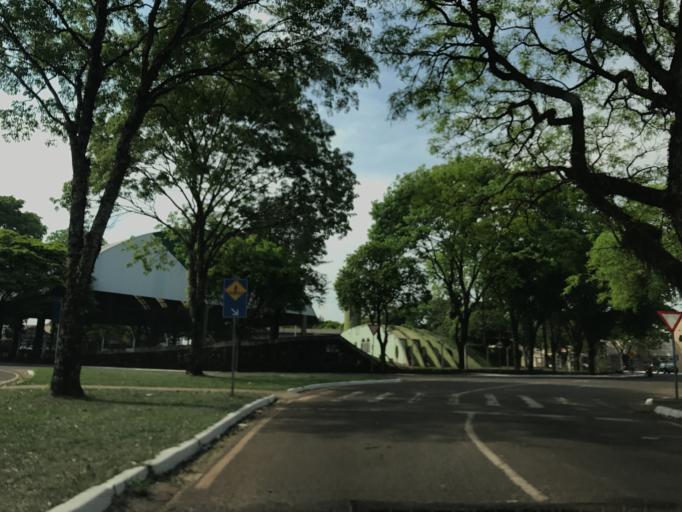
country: BR
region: Parana
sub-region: Maringa
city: Maringa
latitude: -23.4283
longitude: -51.9223
